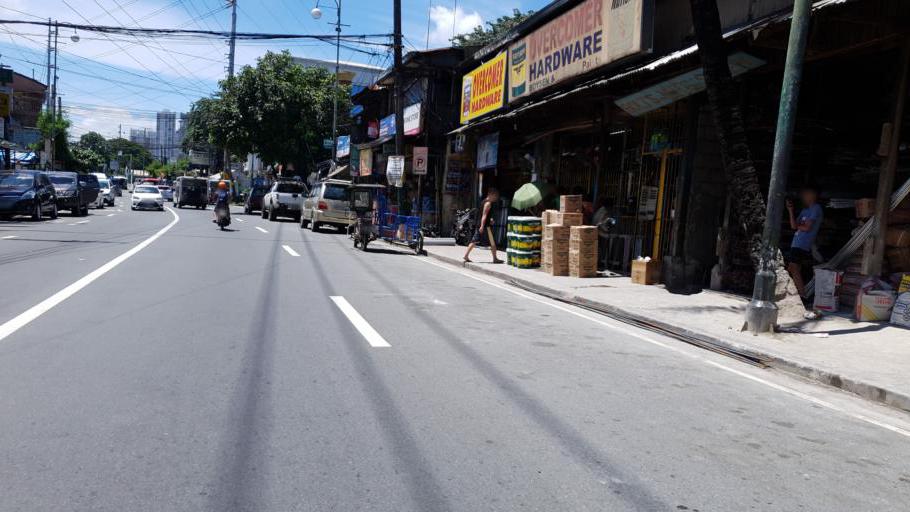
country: PH
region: Metro Manila
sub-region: Pasig
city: Pasig City
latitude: 14.5623
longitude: 121.0609
